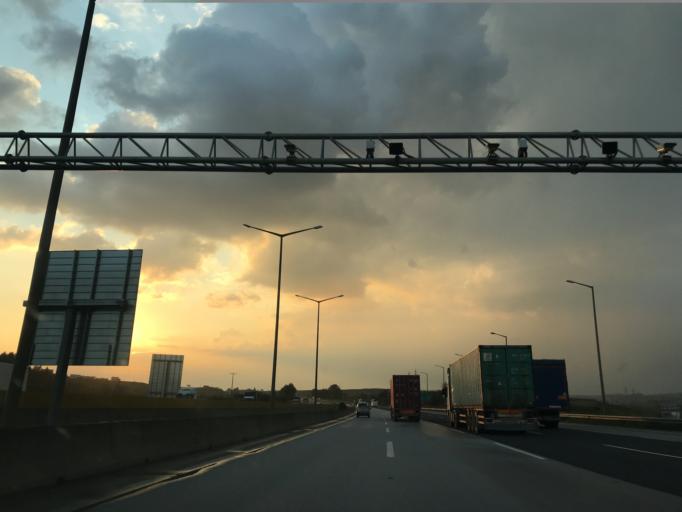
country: TR
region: Mersin
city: Yenice
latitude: 37.0396
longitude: 35.1654
